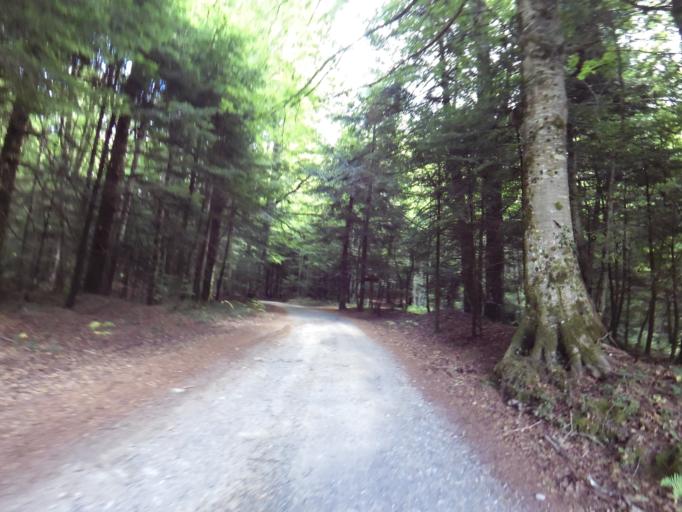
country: IT
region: Calabria
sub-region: Provincia di Vibo-Valentia
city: Mongiana
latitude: 38.5385
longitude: 16.3298
